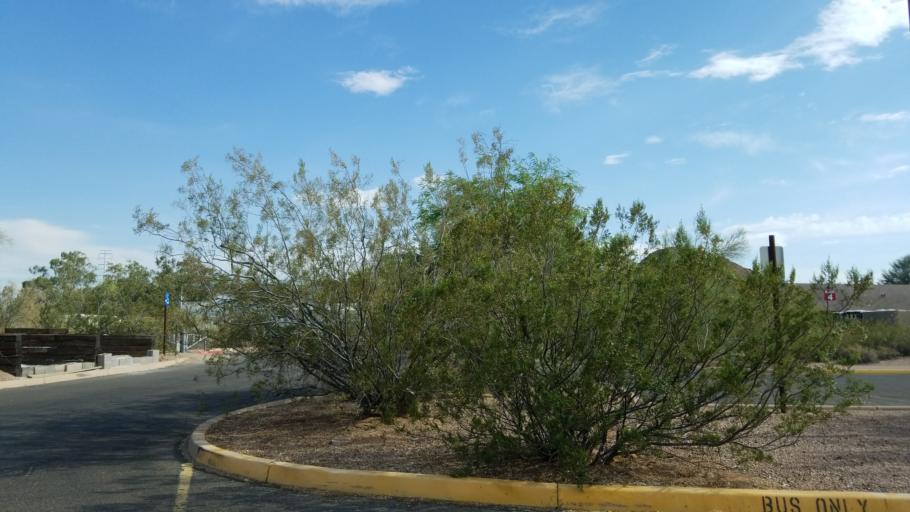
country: US
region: Arizona
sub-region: Maricopa County
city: Tempe Junction
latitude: 33.4621
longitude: -111.9429
